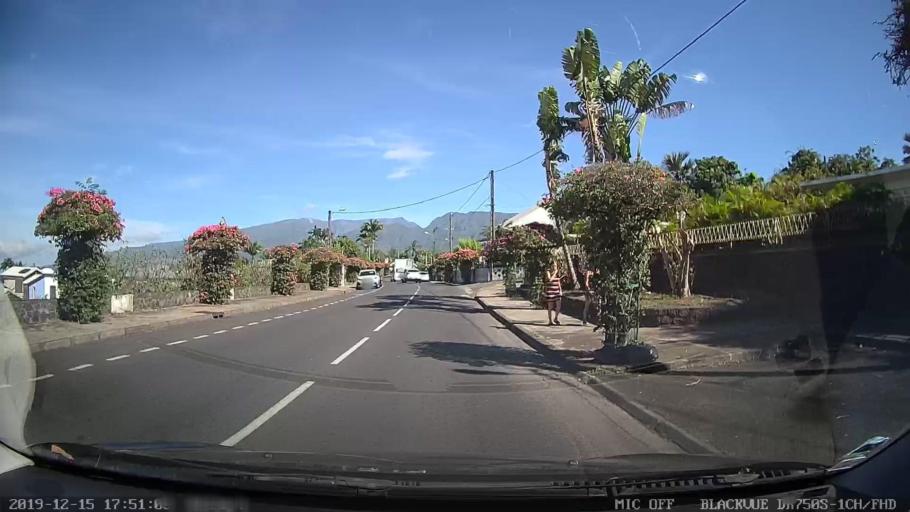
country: RE
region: Reunion
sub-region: Reunion
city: Le Tampon
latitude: -21.2712
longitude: 55.5110
